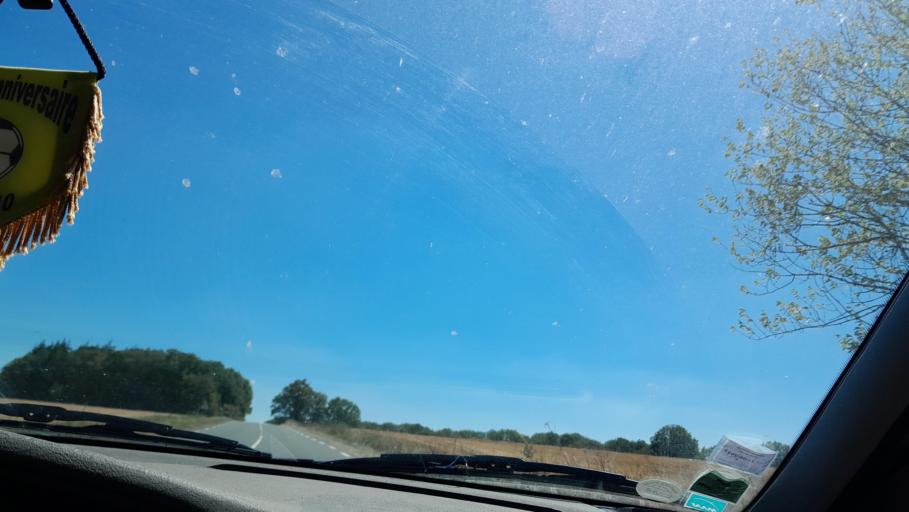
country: FR
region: Pays de la Loire
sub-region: Departement de Maine-et-Loire
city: Pouance
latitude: 47.6971
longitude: -1.1849
